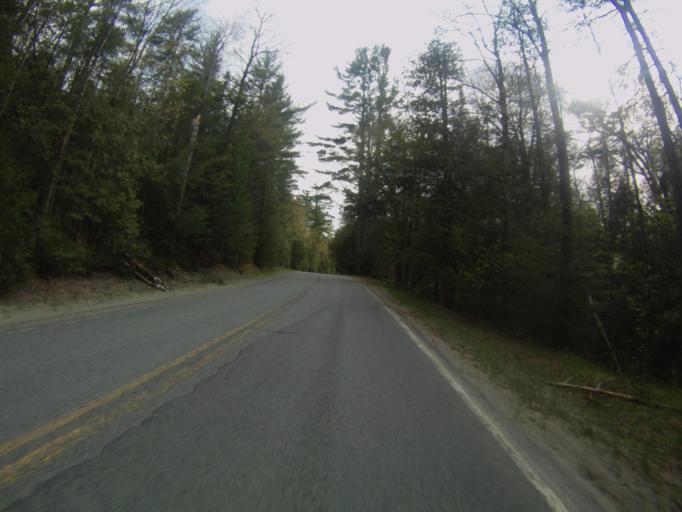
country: US
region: New York
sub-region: Warren County
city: Warrensburg
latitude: 43.8446
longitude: -73.8246
